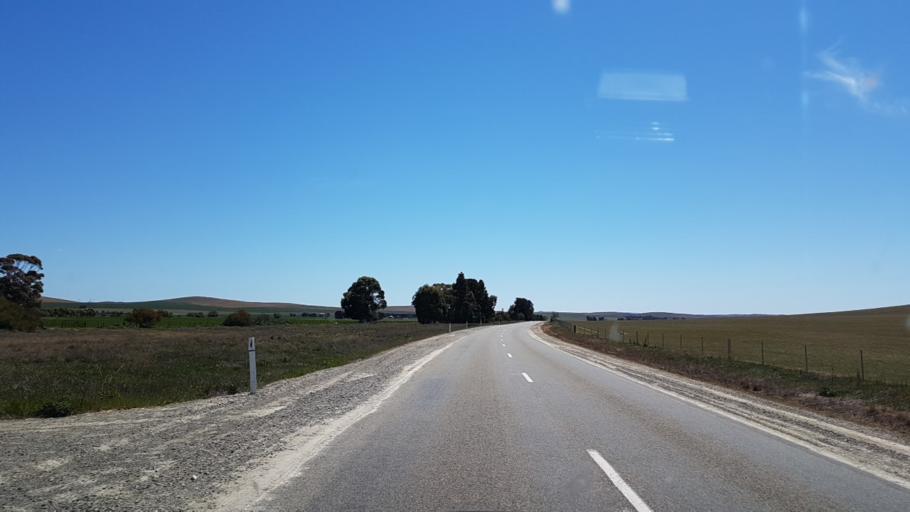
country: AU
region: South Australia
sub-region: Northern Areas
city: Jamestown
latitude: -33.3999
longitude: 138.8900
